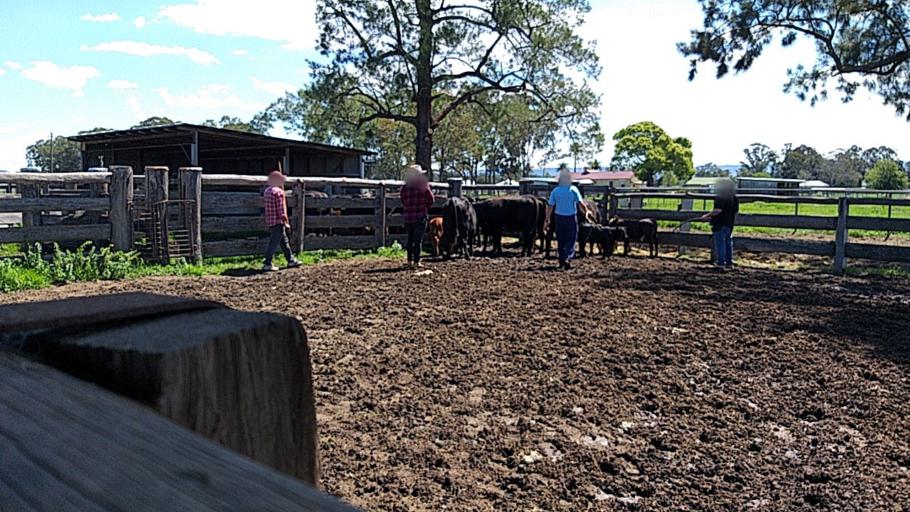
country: AU
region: New South Wales
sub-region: Hawkesbury
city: Richmond
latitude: -33.6179
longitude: 150.7580
